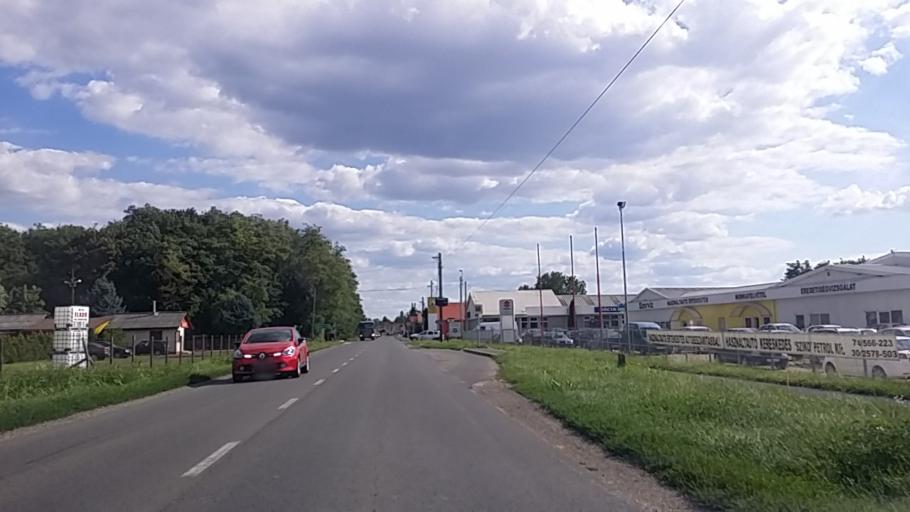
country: HU
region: Tolna
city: Dombovar
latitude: 46.3375
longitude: 18.1270
